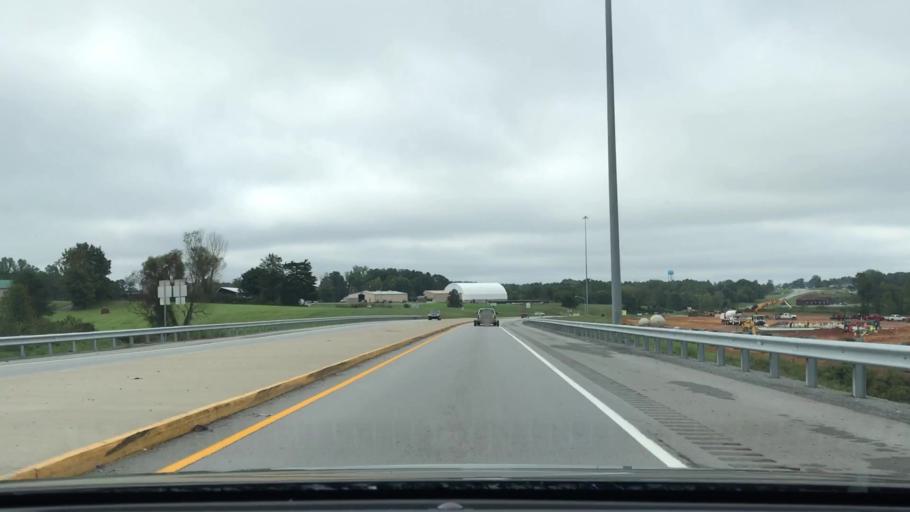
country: US
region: Kentucky
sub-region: Russell County
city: Russell Springs
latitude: 37.0496
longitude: -85.0701
